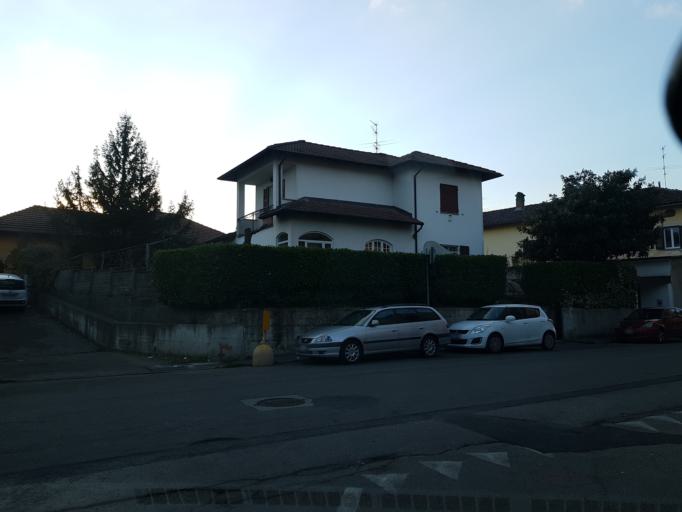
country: IT
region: Piedmont
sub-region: Provincia di Alessandria
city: Novi Ligure
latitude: 44.7586
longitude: 8.7977
